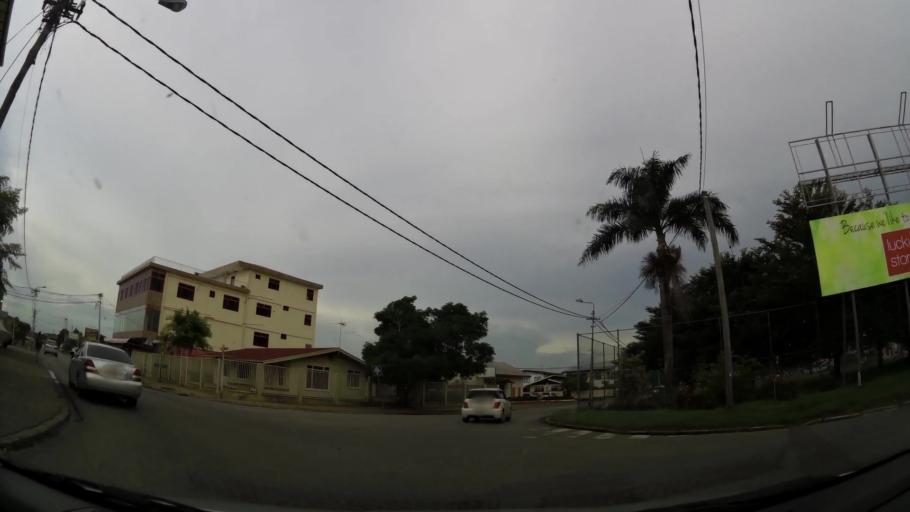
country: SR
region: Paramaribo
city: Paramaribo
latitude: 5.8203
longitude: -55.1836
